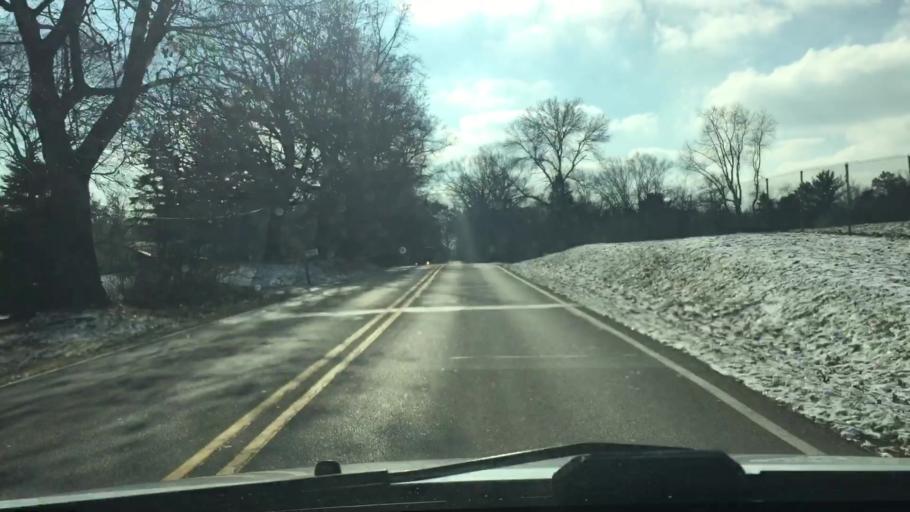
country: US
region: Wisconsin
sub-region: Waukesha County
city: Waukesha
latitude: 42.9834
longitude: -88.2872
